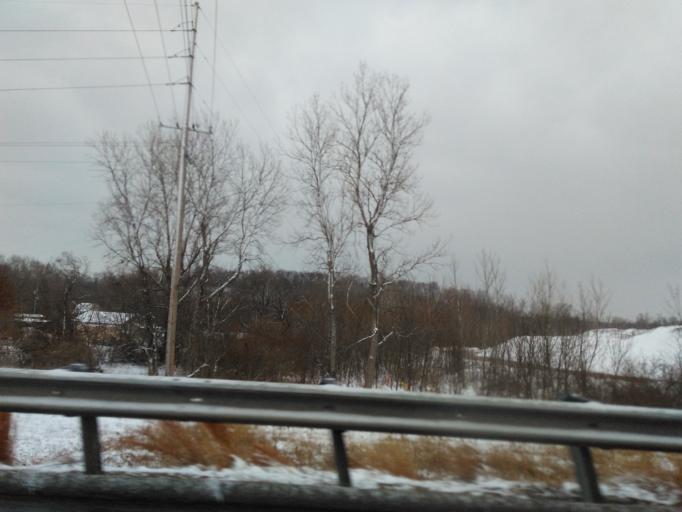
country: US
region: Illinois
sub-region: Saint Clair County
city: Cahokia
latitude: 38.5434
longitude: -90.1739
